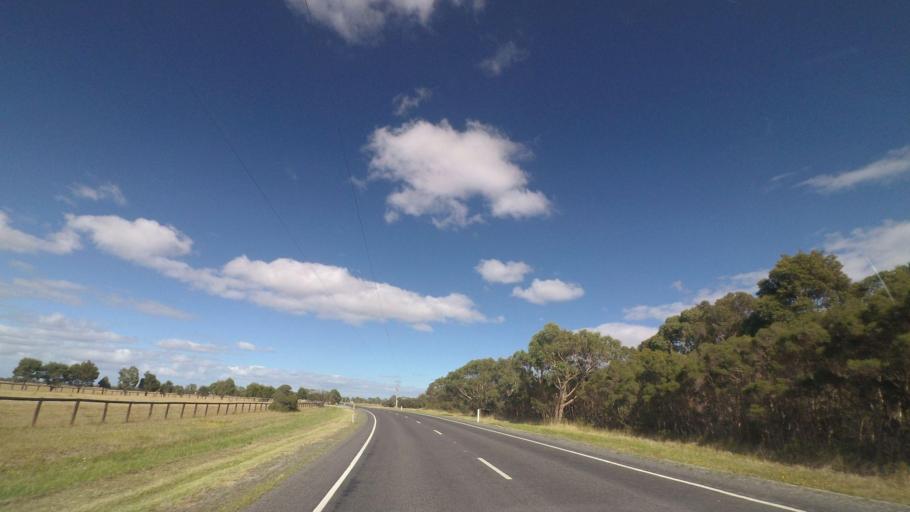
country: AU
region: Victoria
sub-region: Cardinia
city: Koo-Wee-Rup
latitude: -38.1873
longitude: 145.5301
